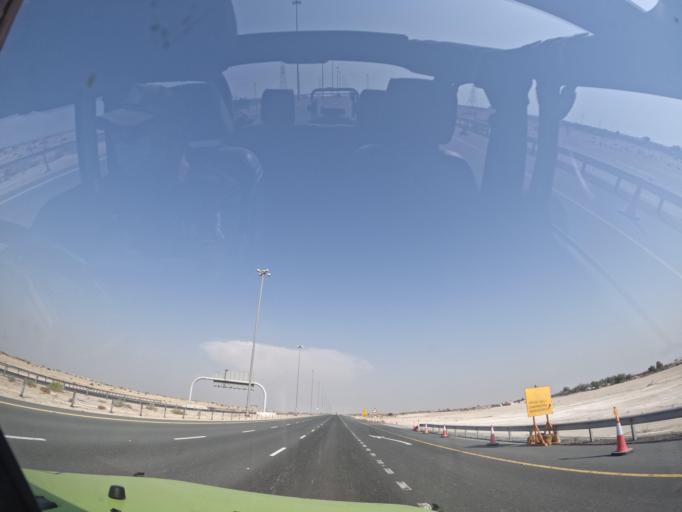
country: AE
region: Abu Dhabi
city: Abu Dhabi
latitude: 24.6770
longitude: 54.8329
